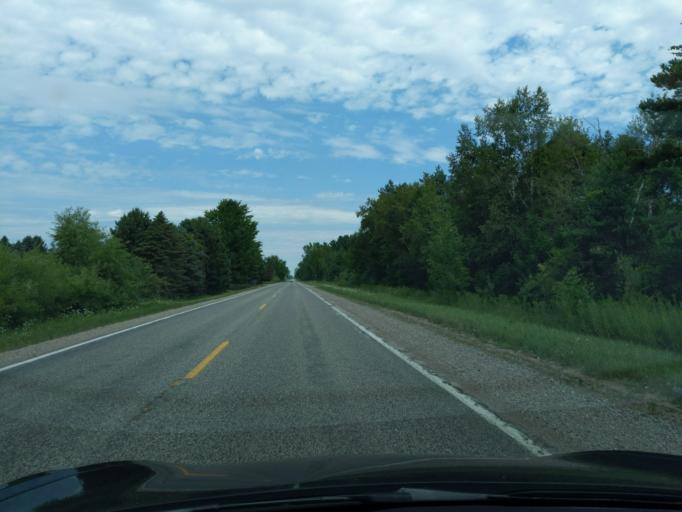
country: US
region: Michigan
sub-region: Gratiot County
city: Breckenridge
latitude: 43.4317
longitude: -84.3700
